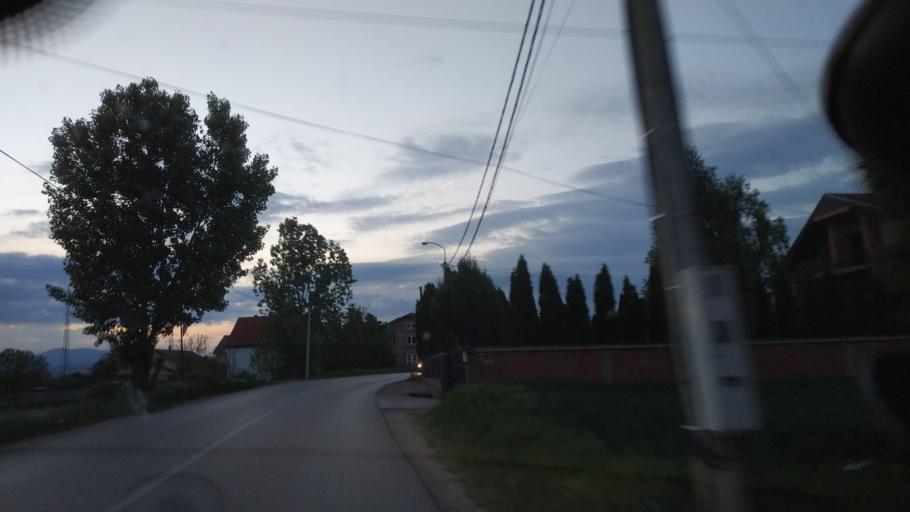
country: RS
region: Central Serbia
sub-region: Nisavski Okrug
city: Merosina
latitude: 43.2860
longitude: 21.7186
